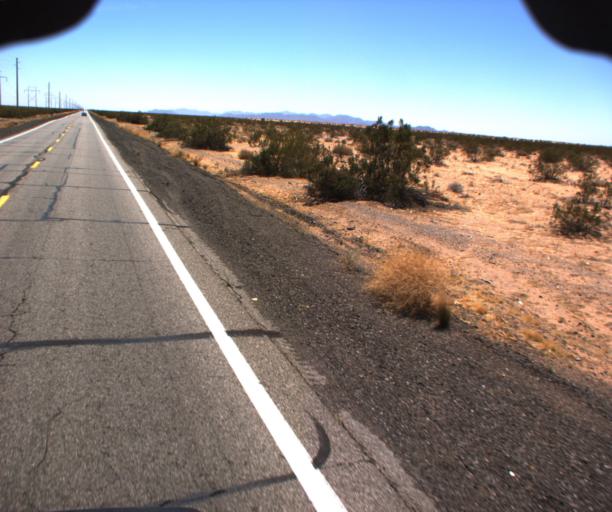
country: US
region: Arizona
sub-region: La Paz County
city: Parker
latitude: 33.9125
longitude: -114.2169
